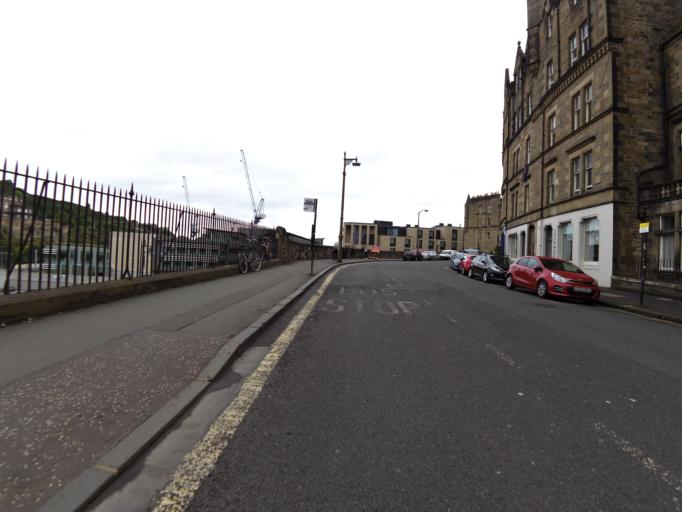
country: GB
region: Scotland
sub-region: Edinburgh
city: Edinburgh
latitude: 55.9514
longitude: -3.1856
